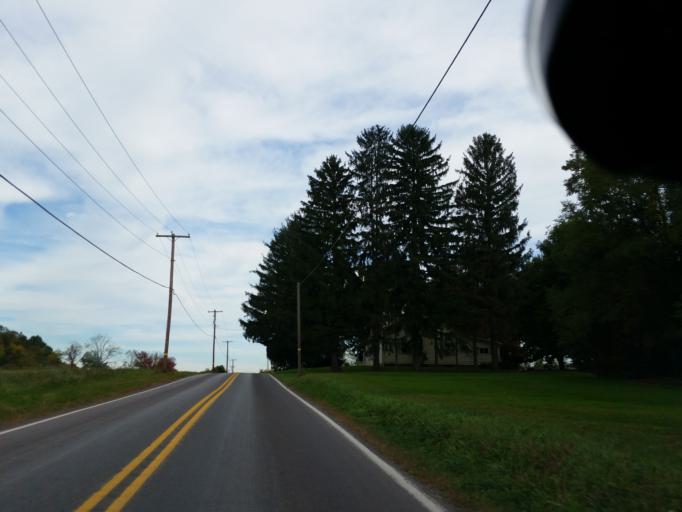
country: US
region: Pennsylvania
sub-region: Lycoming County
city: Duboistown
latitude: 41.1248
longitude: -77.0043
